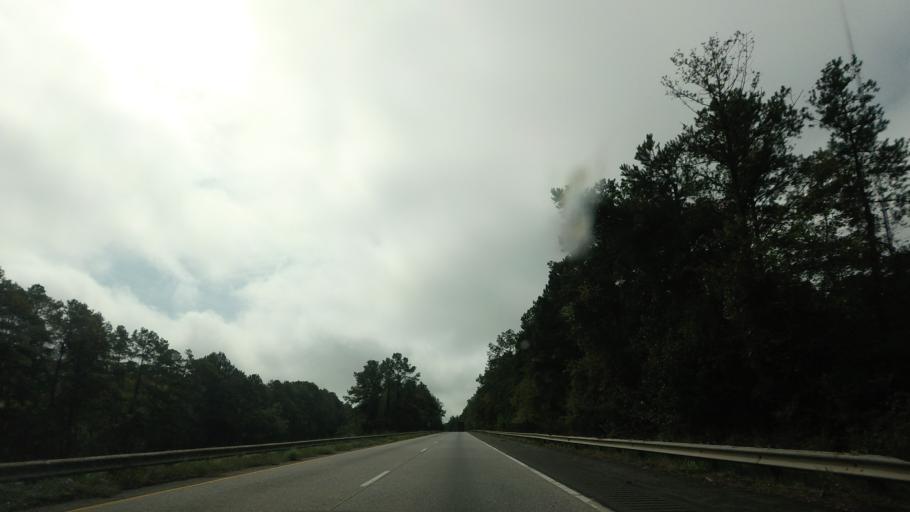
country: US
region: Georgia
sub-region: Bibb County
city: Macon
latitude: 32.7669
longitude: -83.5569
